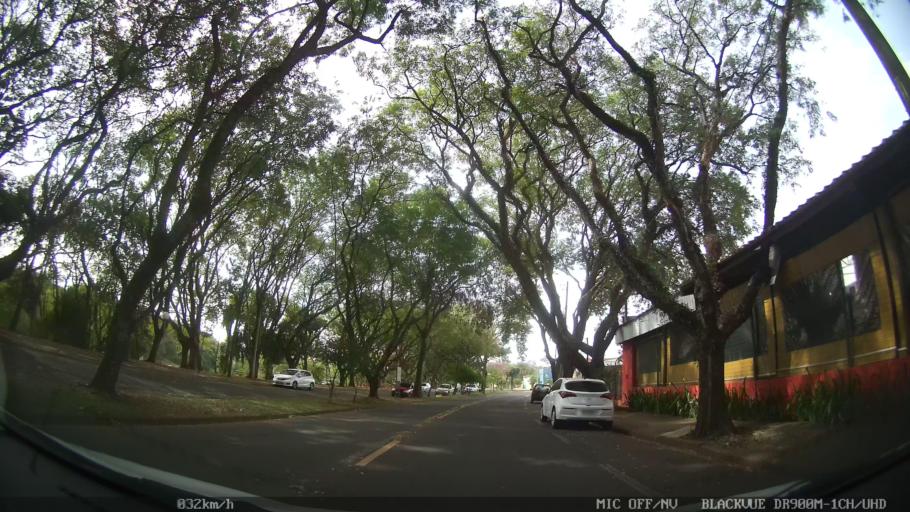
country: BR
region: Sao Paulo
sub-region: Piracicaba
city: Piracicaba
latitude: -22.7053
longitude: -47.6742
